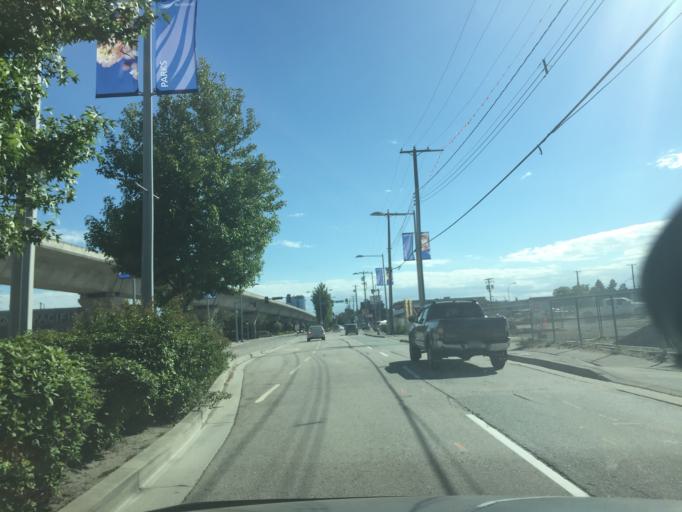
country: CA
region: British Columbia
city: Richmond
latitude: 49.1899
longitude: -123.1316
